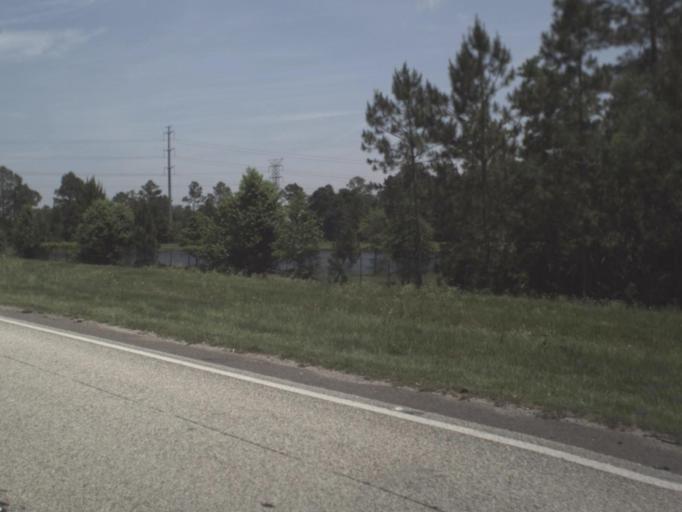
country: US
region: Florida
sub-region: Duval County
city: Neptune Beach
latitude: 30.2921
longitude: -81.5217
